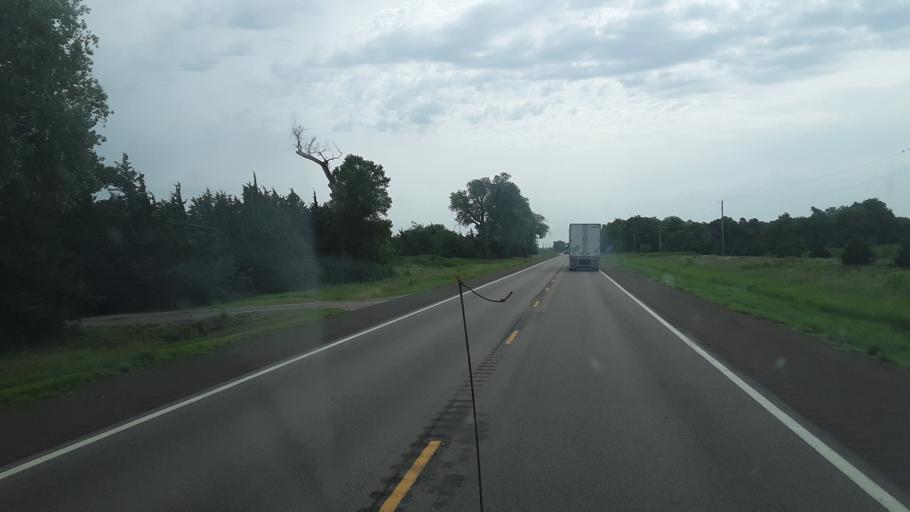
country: US
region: Kansas
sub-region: Stafford County
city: Saint John
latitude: 37.9557
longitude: -98.7156
